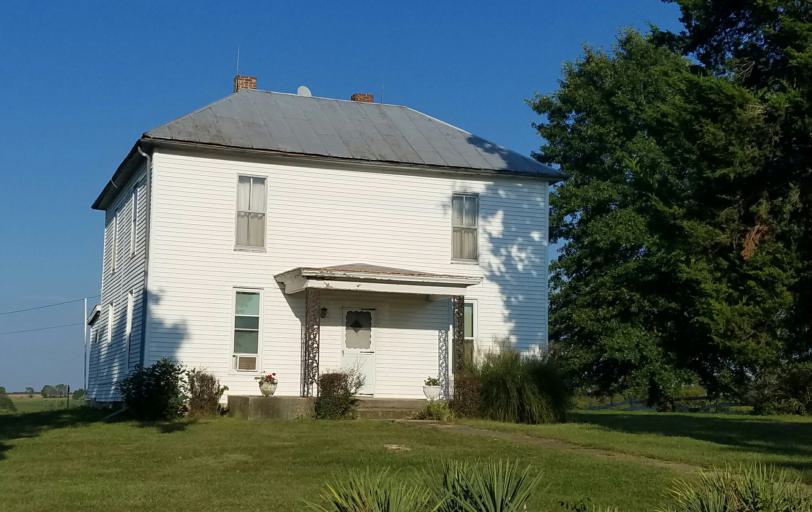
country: US
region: Missouri
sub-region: Moniteau County
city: California
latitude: 38.6437
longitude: -92.5699
